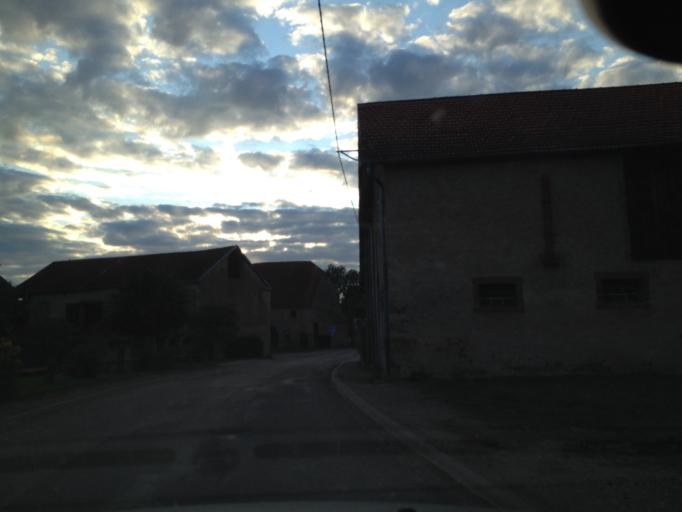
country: FR
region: Franche-Comte
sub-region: Departement de la Haute-Saone
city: Saint-Loup-sur-Semouse
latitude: 47.9332
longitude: 6.1680
